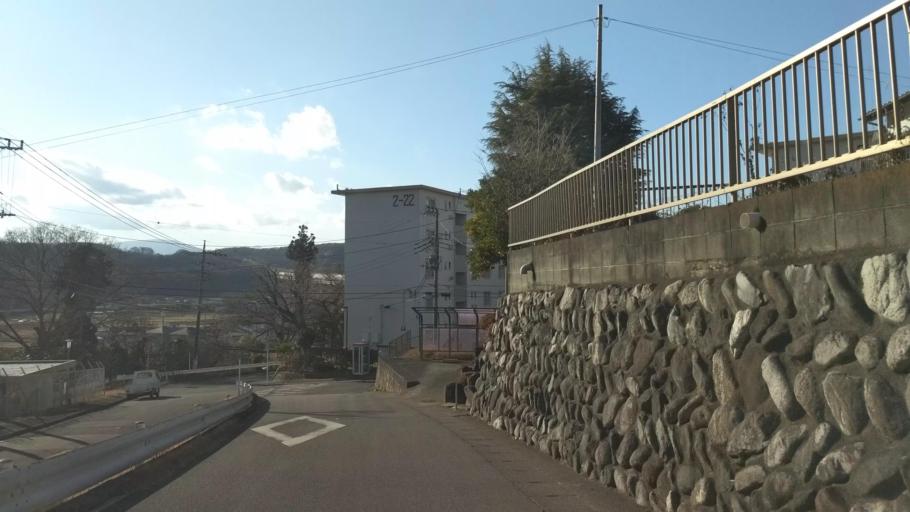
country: JP
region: Kanagawa
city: Hadano
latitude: 35.3614
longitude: 139.2576
